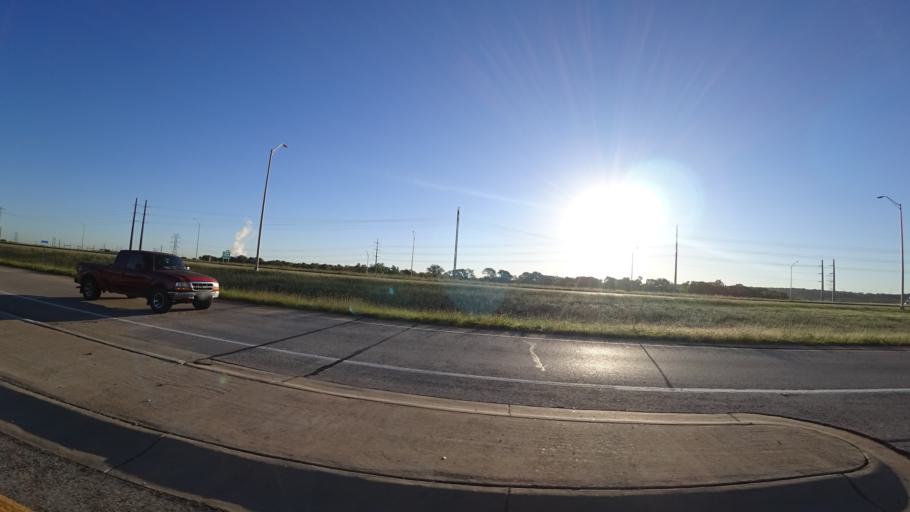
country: US
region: Texas
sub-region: Travis County
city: Hornsby Bend
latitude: 30.2038
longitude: -97.6233
